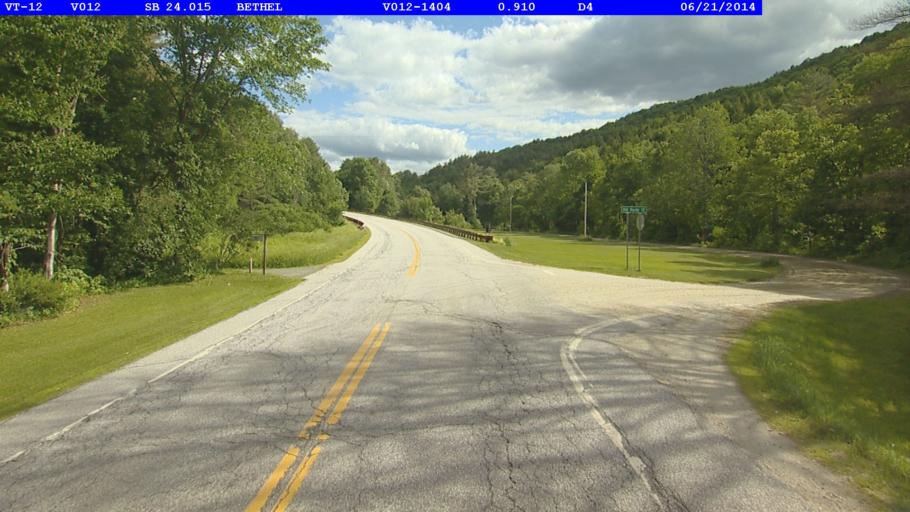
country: US
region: Vermont
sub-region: Orange County
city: Randolph
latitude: 43.8033
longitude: -72.6532
